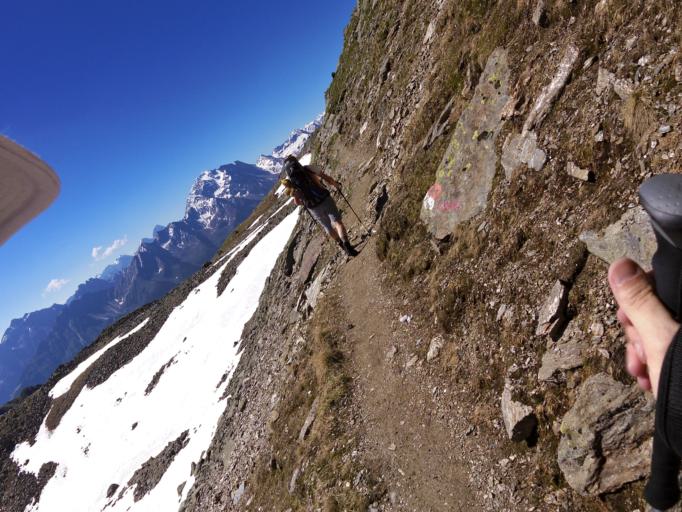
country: AT
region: Tyrol
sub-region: Politischer Bezirk Innsbruck Land
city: Neustift im Stubaital
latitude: 47.1411
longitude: 11.2616
